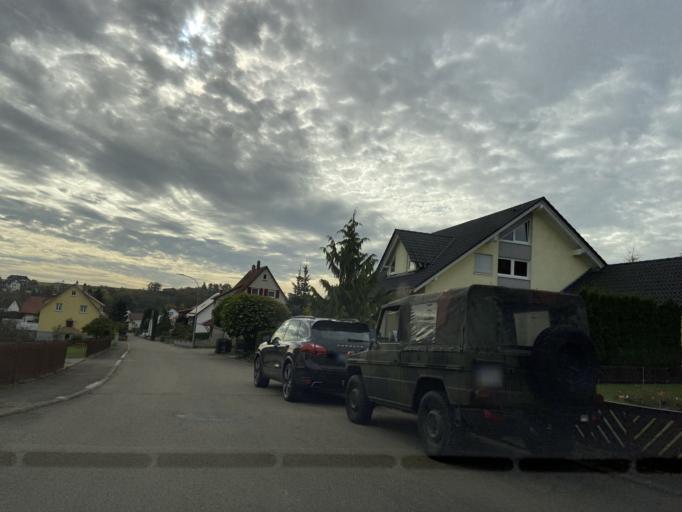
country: DE
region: Baden-Wuerttemberg
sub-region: Tuebingen Region
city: Bingen
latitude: 48.1116
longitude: 9.2669
